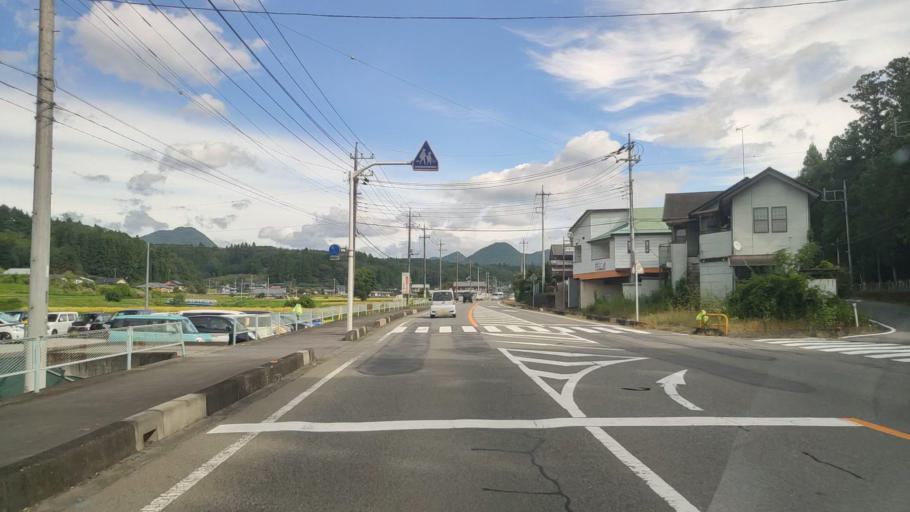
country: JP
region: Gunma
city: Nakanojomachi
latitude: 36.5929
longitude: 138.8615
